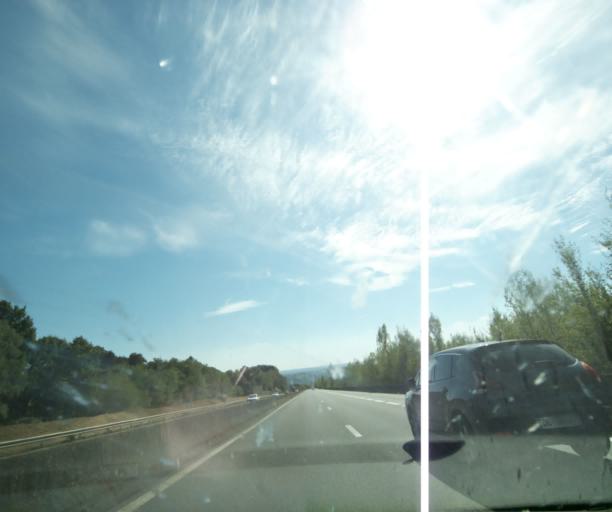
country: FR
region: Limousin
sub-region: Departement de la Correze
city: Donzenac
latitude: 45.2413
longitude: 1.5126
